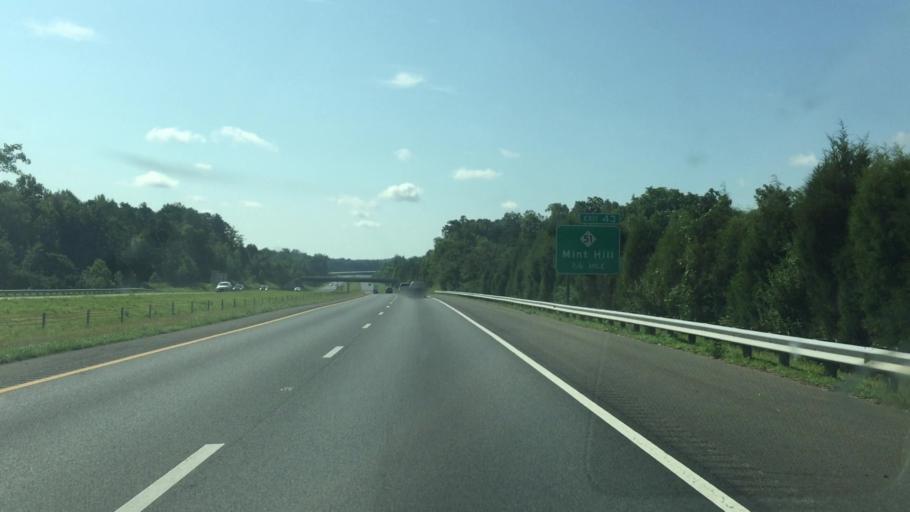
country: US
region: North Carolina
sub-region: Mecklenburg County
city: Mint Hill
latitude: 35.2126
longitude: -80.6442
